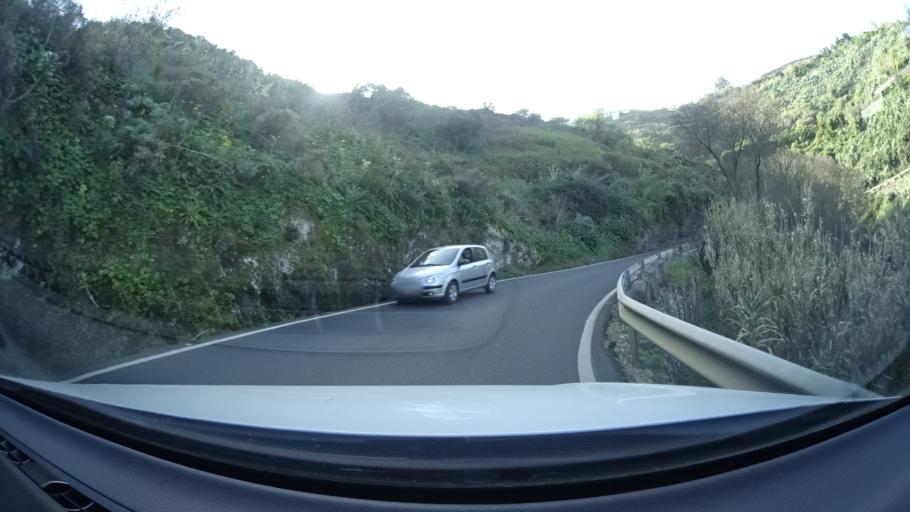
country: ES
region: Canary Islands
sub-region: Provincia de Las Palmas
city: Valleseco
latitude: 28.0249
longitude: -15.5559
